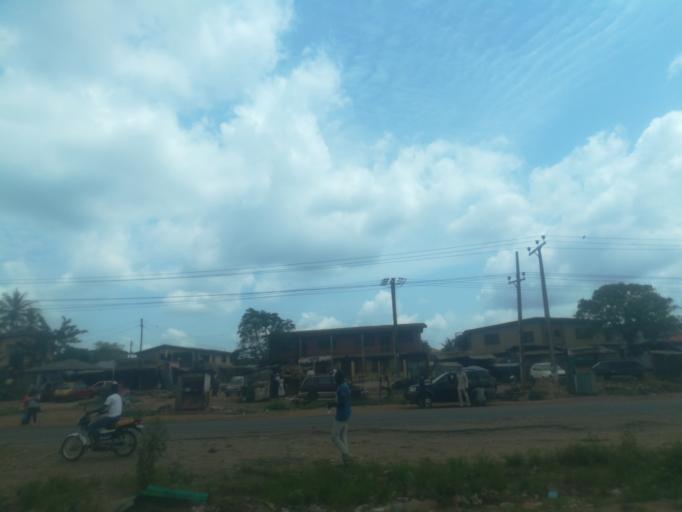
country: NG
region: Oyo
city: Ibadan
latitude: 7.4141
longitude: 3.9426
